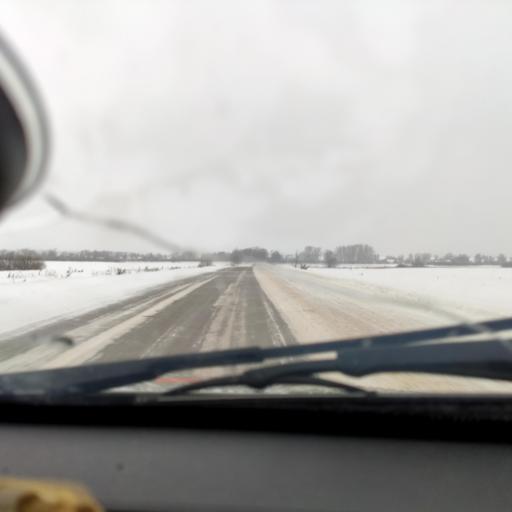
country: RU
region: Bashkortostan
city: Avdon
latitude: 54.5770
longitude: 55.8691
